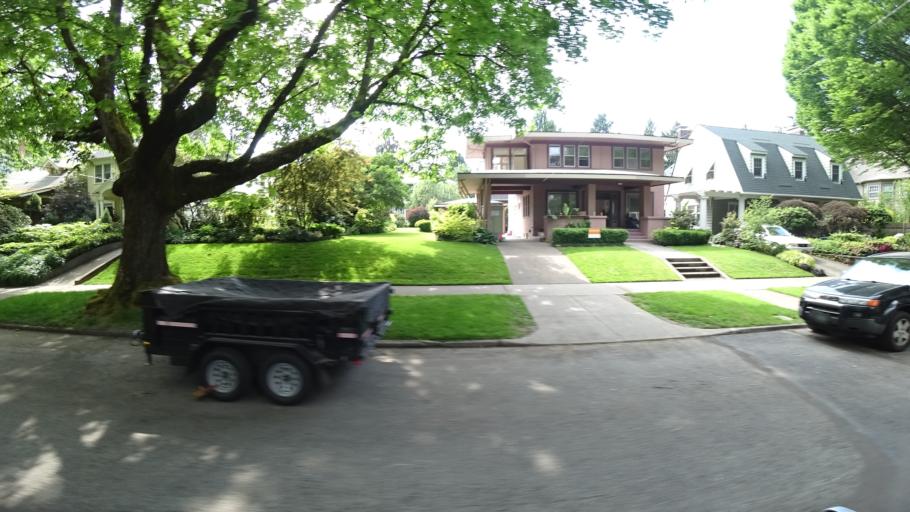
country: US
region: Oregon
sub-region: Multnomah County
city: Portland
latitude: 45.5445
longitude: -122.6484
